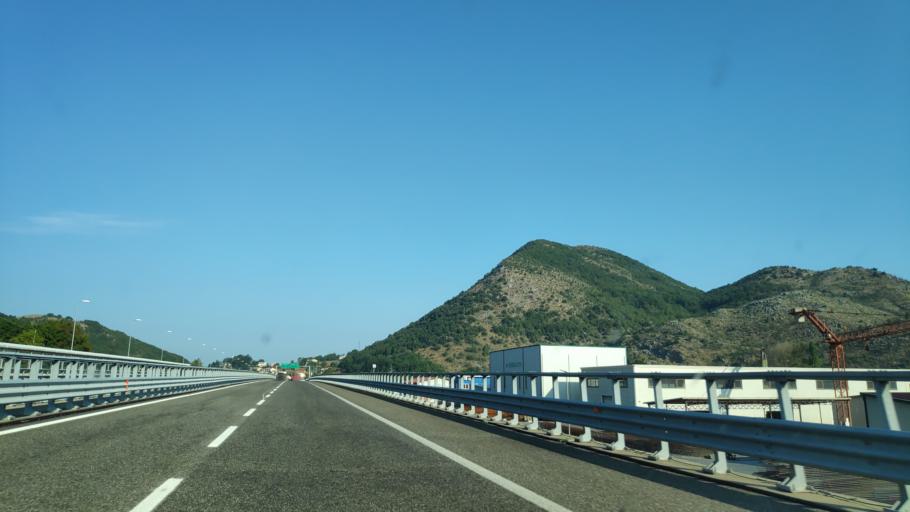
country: IT
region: Basilicate
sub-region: Provincia di Potenza
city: Lauria
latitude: 40.0148
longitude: 15.8959
